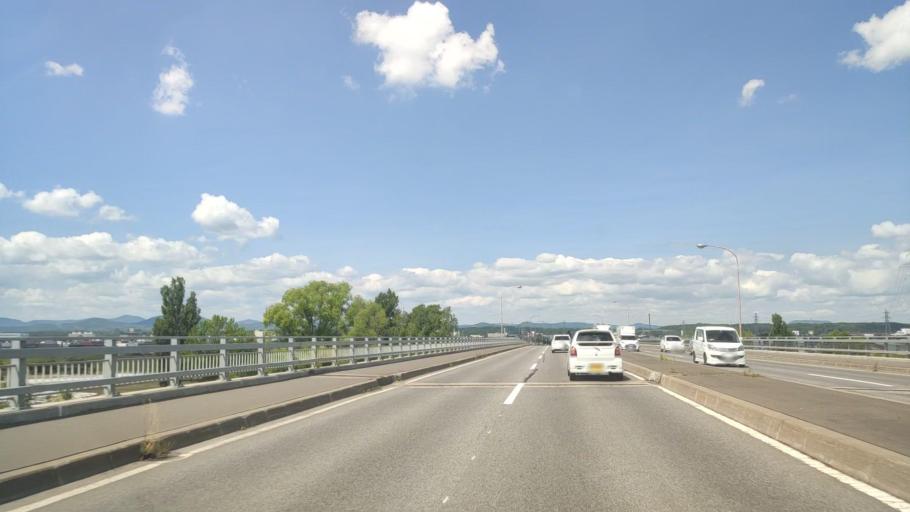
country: JP
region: Hokkaido
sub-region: Asahikawa-shi
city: Asahikawa
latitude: 43.7974
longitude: 142.3966
